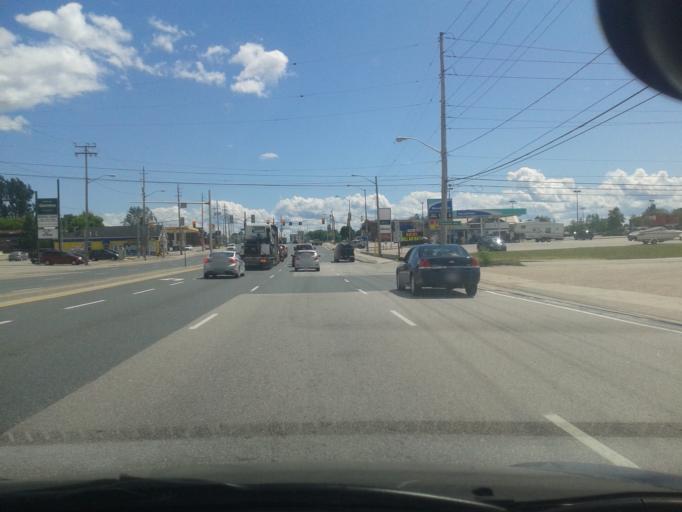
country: CA
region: Ontario
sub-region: Nipissing District
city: North Bay
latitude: 46.3329
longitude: -79.4662
